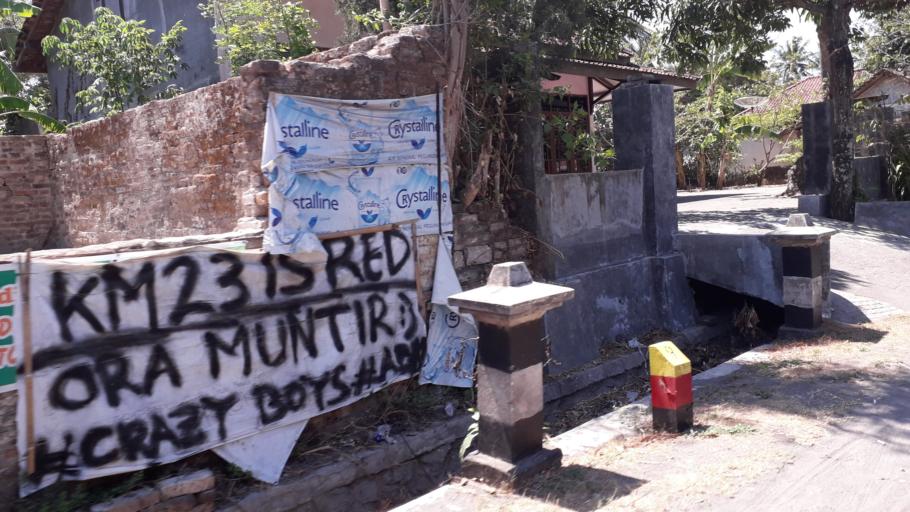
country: ID
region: Daerah Istimewa Yogyakarta
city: Pundong
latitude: -7.9866
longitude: 110.3155
